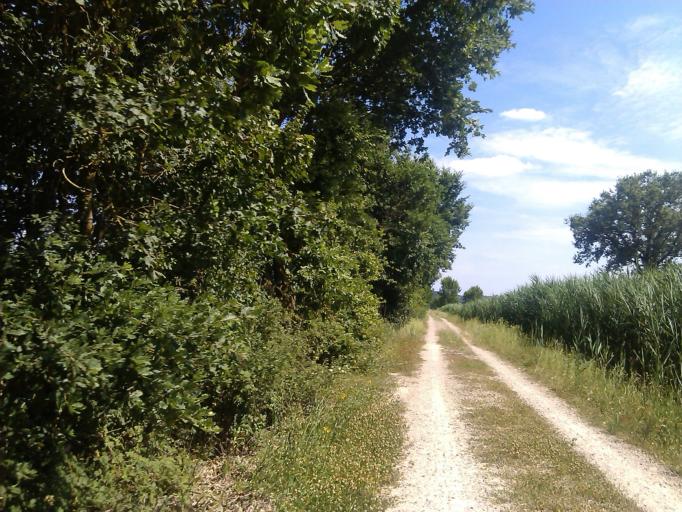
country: IT
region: Tuscany
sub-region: Provincia di Siena
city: Chiusi
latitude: 43.0681
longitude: 11.9288
